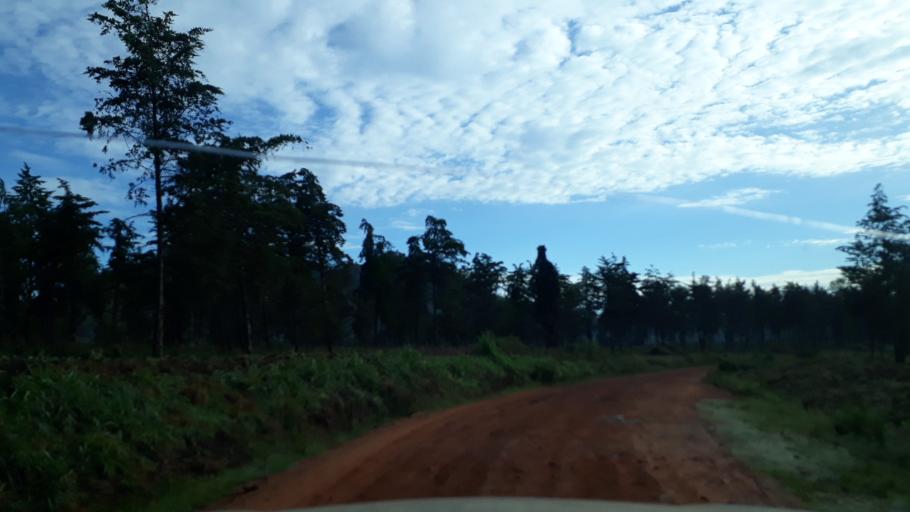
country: UG
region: Northern Region
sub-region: Zombo District
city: Paidha
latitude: 2.2514
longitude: 30.8666
